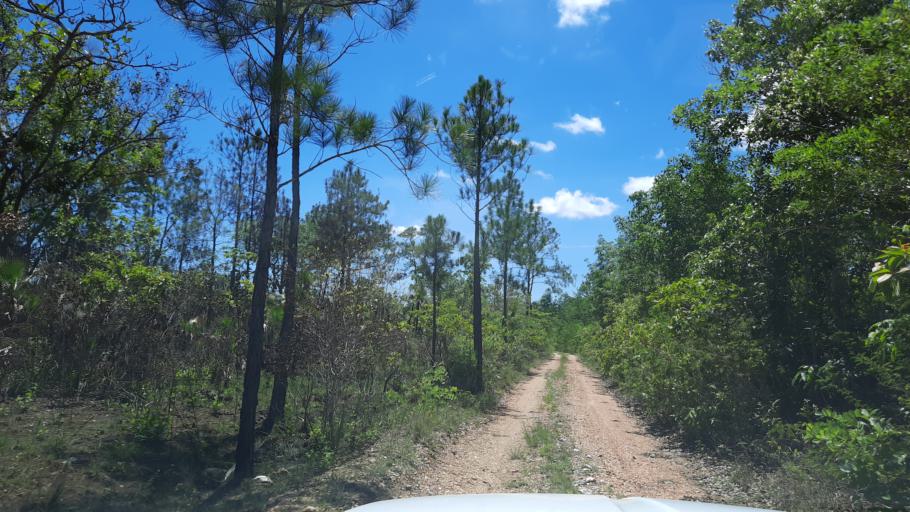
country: BZ
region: Cayo
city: Belmopan
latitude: 17.3583
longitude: -88.5363
